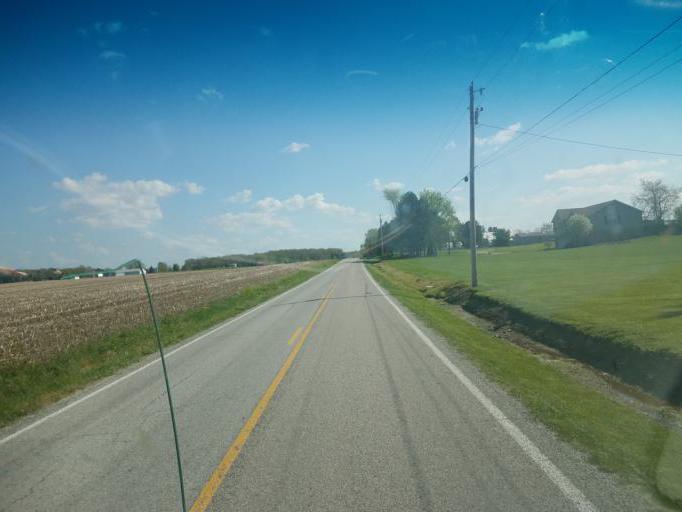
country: US
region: Ohio
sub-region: Medina County
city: Westfield Center
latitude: 40.9807
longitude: -81.9580
